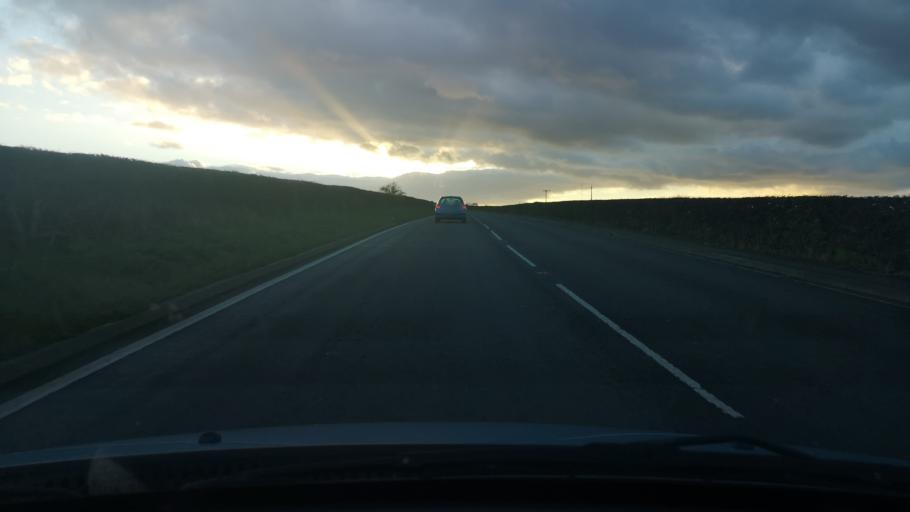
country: GB
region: England
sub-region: City and Borough of Wakefield
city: Horbury
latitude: 53.6282
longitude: -1.5704
